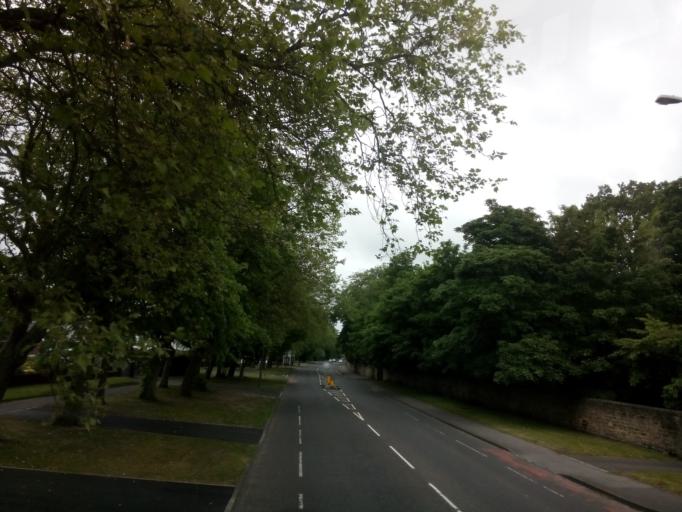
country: GB
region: England
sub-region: County Durham
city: Chester-le-Street
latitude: 54.8693
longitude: -1.5748
